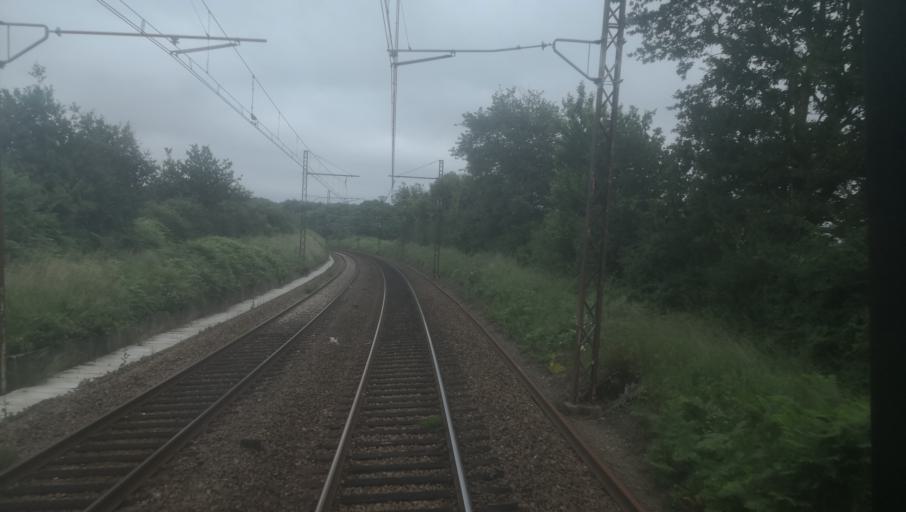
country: FR
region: Centre
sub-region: Departement de l'Indre
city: Chantome
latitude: 46.4774
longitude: 1.5379
